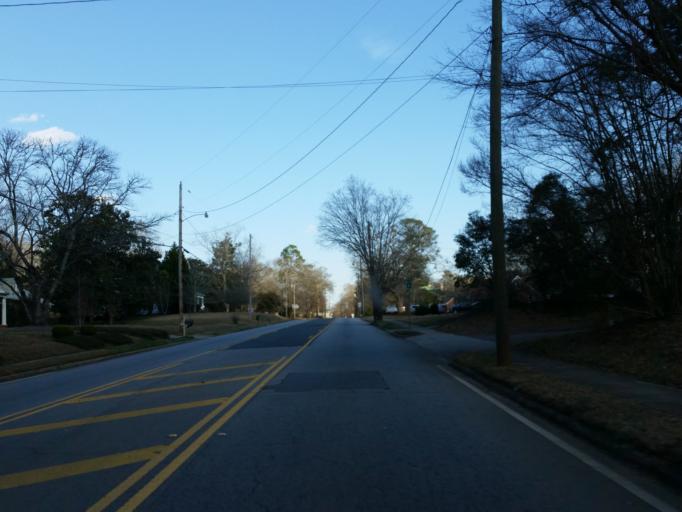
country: US
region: Georgia
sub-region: Monroe County
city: Forsyth
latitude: 33.0345
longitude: -83.9498
